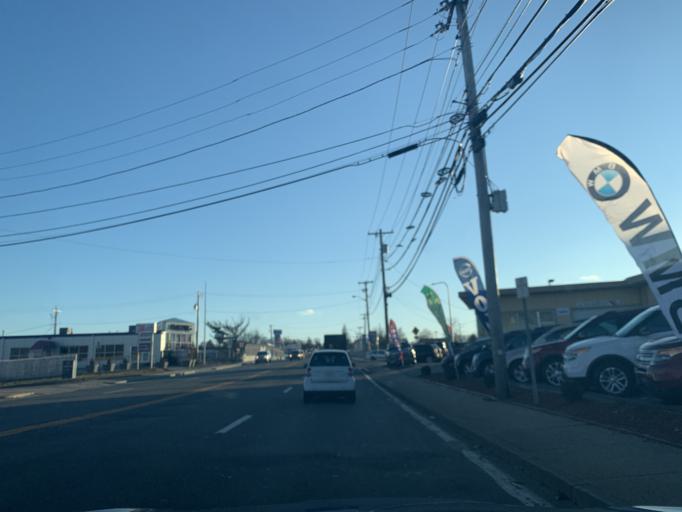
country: US
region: Rhode Island
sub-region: Providence County
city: East Providence
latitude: 41.8134
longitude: -71.3581
